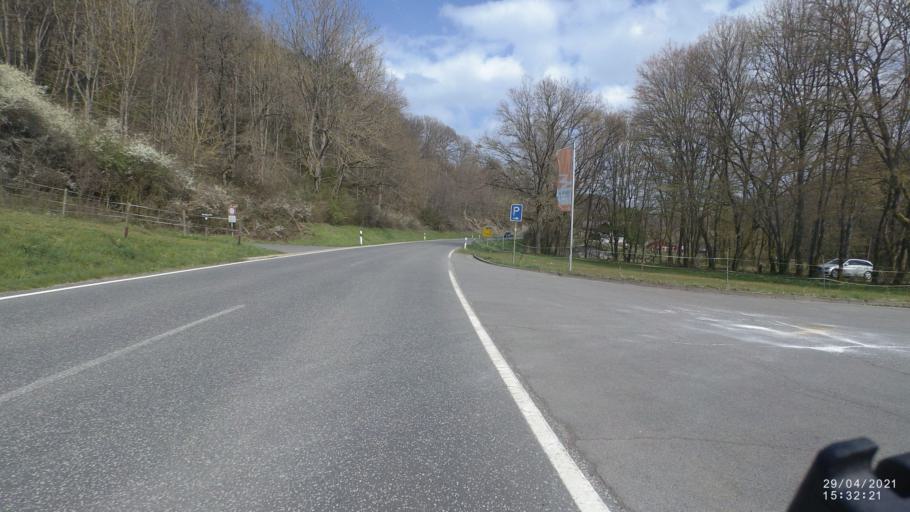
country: DE
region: Rheinland-Pfalz
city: Volkesfeld
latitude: 50.3843
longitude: 7.1454
